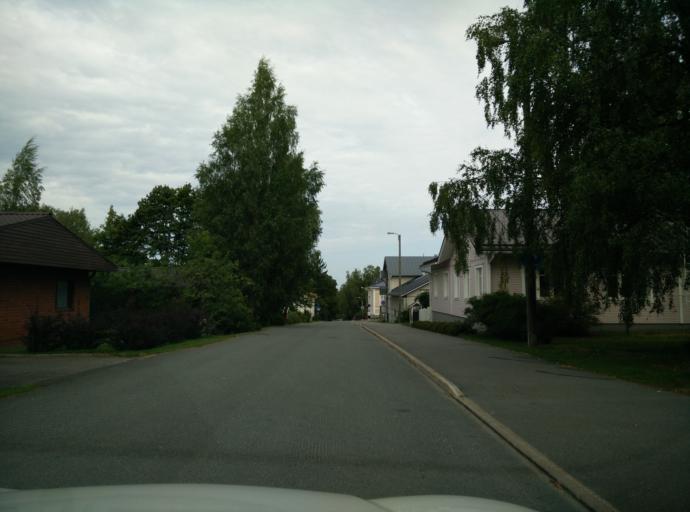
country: FI
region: Haeme
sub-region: Haemeenlinna
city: Haemeenlinna
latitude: 60.9906
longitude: 24.4458
